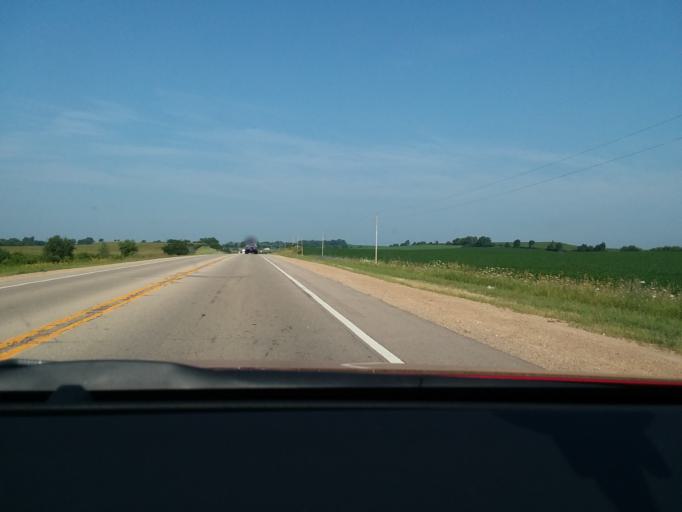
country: US
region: Wisconsin
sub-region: Dane County
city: Windsor
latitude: 43.1956
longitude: -89.3702
